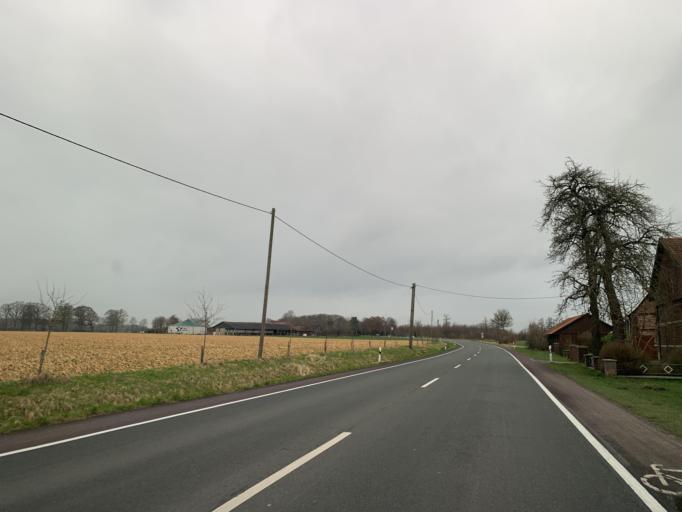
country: DE
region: North Rhine-Westphalia
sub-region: Regierungsbezirk Munster
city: Senden
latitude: 51.8769
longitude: 7.4591
